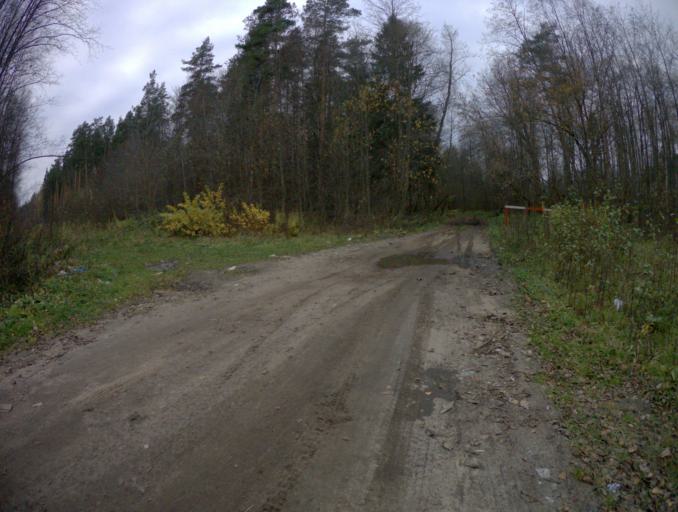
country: RU
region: Moskovskaya
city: Vereya
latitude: 55.8735
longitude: 39.0661
